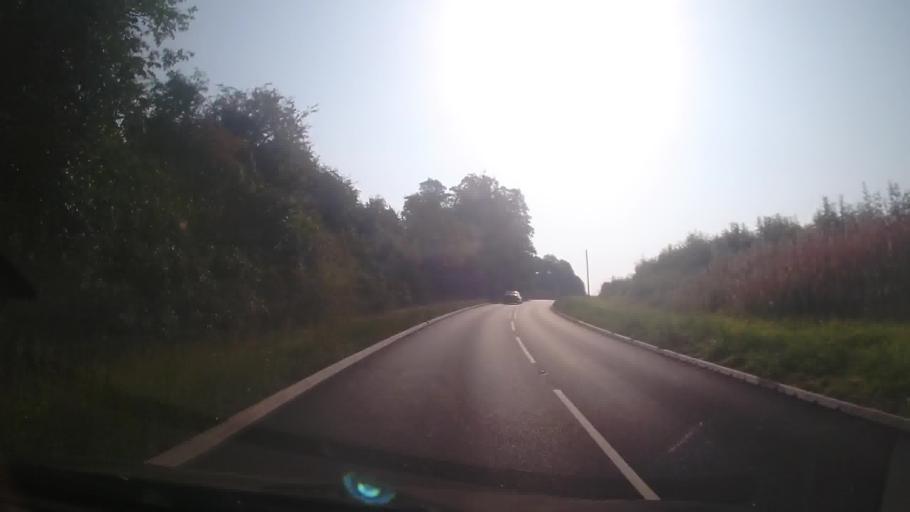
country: GB
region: England
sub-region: Shropshire
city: Broseley
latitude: 52.5498
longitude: -2.4938
